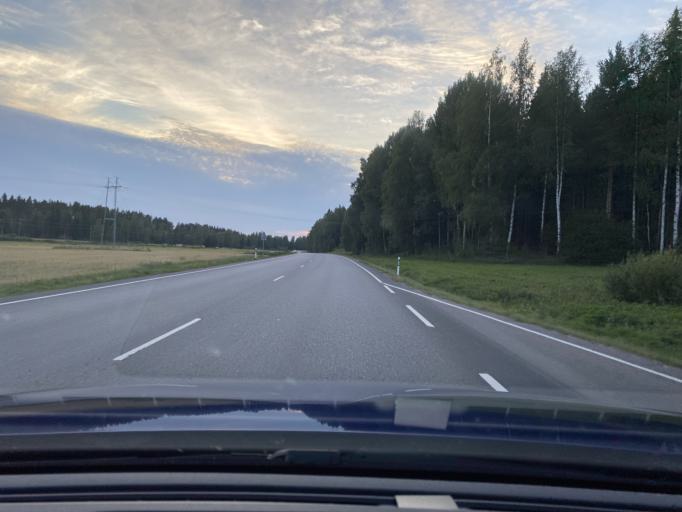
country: FI
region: Satakunta
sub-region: Pohjois-Satakunta
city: Kankaanpaeae
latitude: 61.7791
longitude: 22.4472
